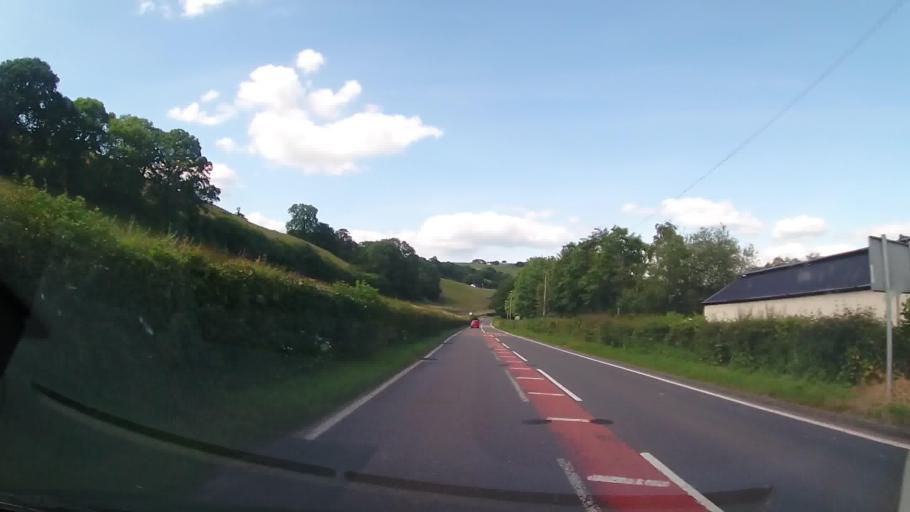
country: GB
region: Wales
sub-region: Sir Powys
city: Llanfyllin
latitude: 52.6529
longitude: -3.3216
